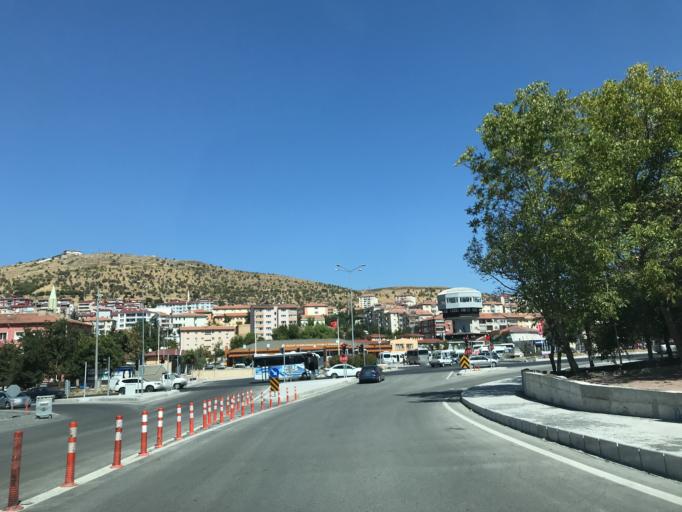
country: TR
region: Yozgat
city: Yozgat
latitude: 39.8222
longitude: 34.8174
